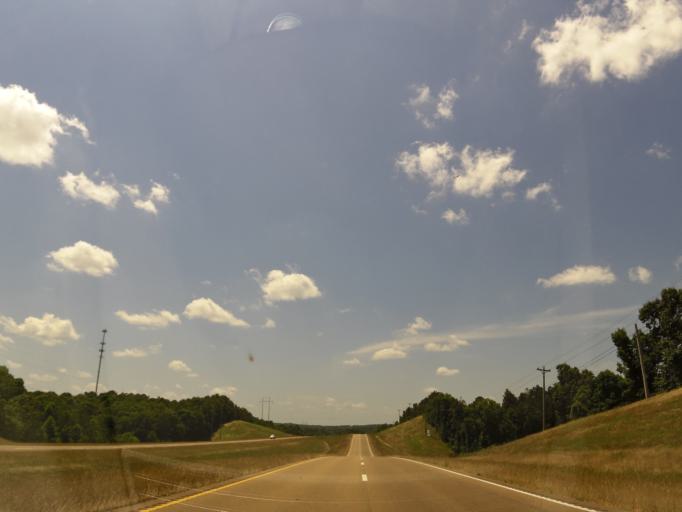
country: US
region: Mississippi
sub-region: Lafayette County
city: Oxford
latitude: 34.3222
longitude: -89.3778
